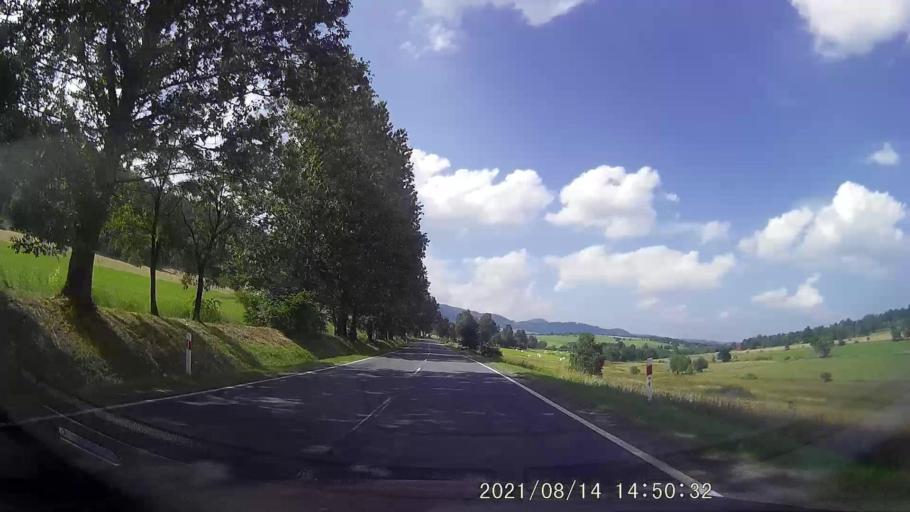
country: PL
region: Lower Silesian Voivodeship
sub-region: Powiat walbrzyski
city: Gluszyca Gorna
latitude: 50.6530
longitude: 16.3788
